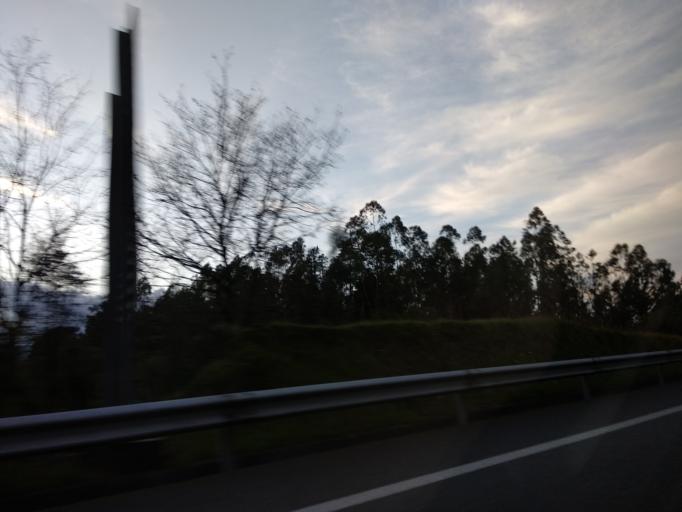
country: PT
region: Braga
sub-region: Braga
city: Oliveira
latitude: 41.5048
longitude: -8.4723
